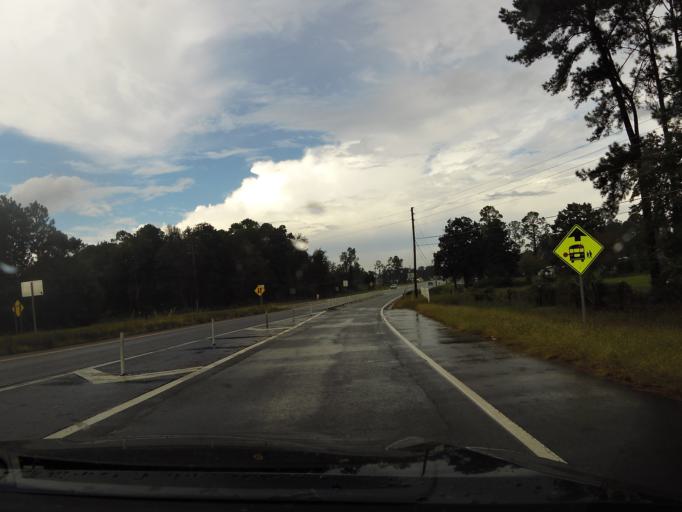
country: US
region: Georgia
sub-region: Wayne County
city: Jesup
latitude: 31.6253
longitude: -81.8671
